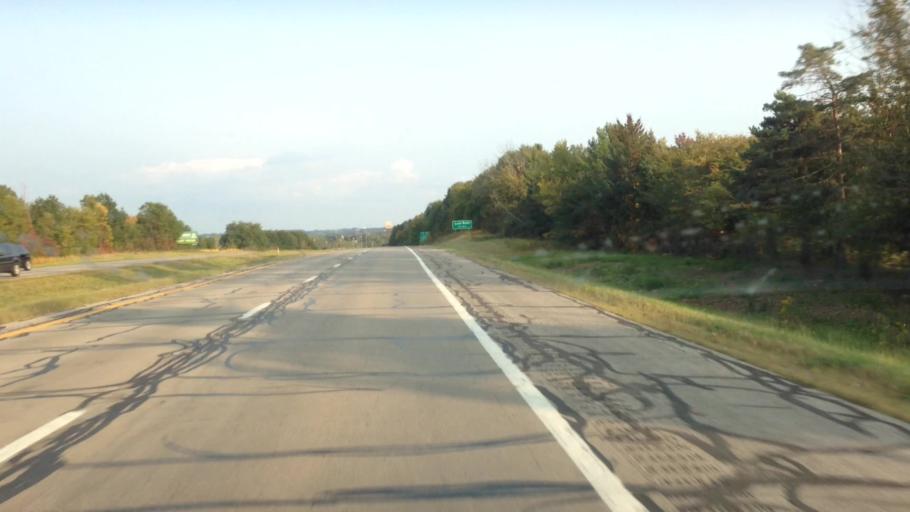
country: US
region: Ohio
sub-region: Medina County
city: Westfield Center
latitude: 41.0350
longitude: -81.9169
